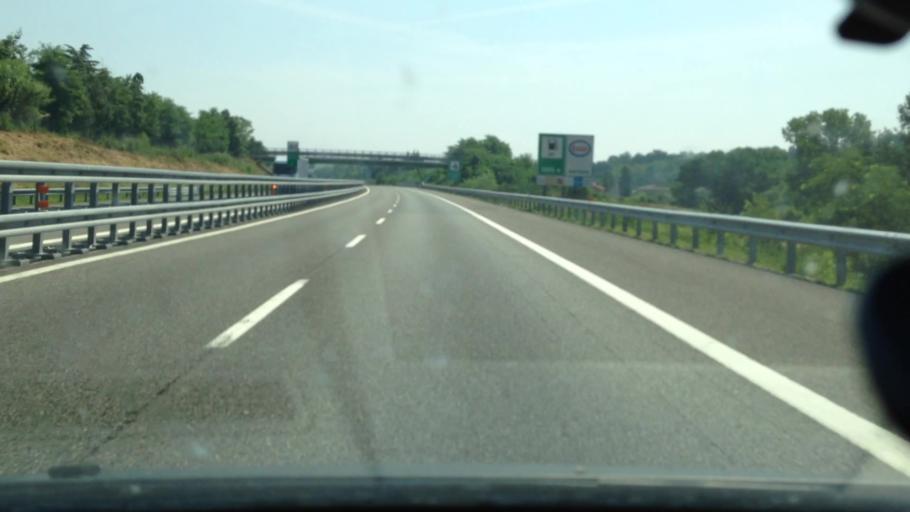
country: IT
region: Piedmont
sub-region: Provincia di Asti
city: Cerro Tanaro
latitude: 44.9036
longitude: 8.3494
